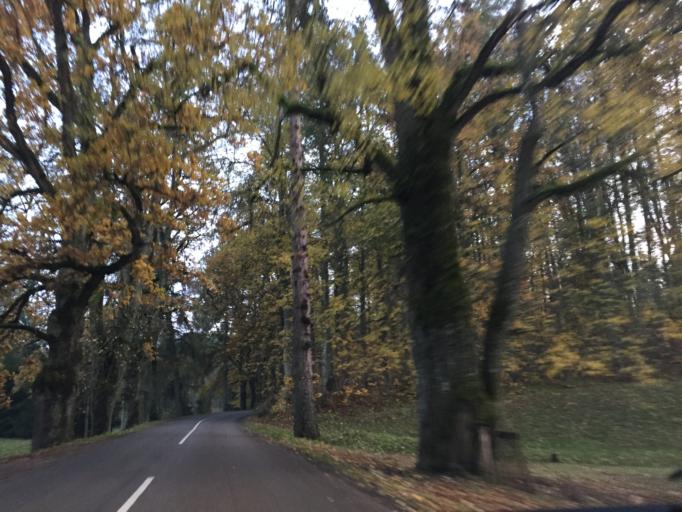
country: LV
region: Cesu Rajons
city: Cesis
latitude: 57.3084
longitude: 25.1650
